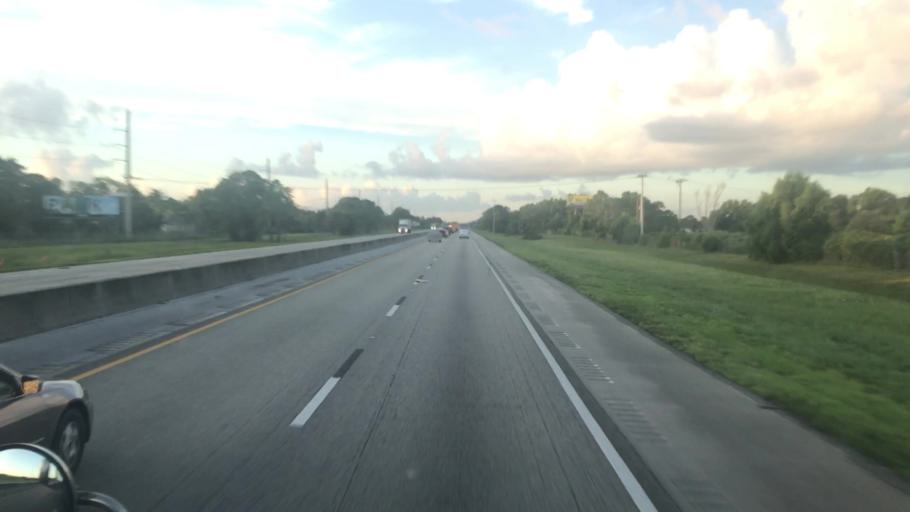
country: US
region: Florida
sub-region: Saint Lucie County
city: Port Saint Lucie
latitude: 27.2511
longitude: -80.3480
